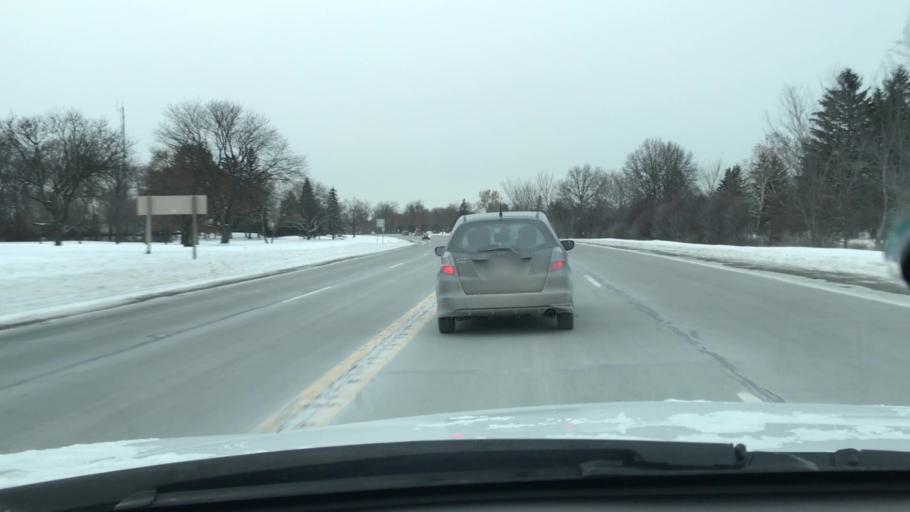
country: US
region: Michigan
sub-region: Oakland County
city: Pontiac
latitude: 42.6529
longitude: -83.3278
